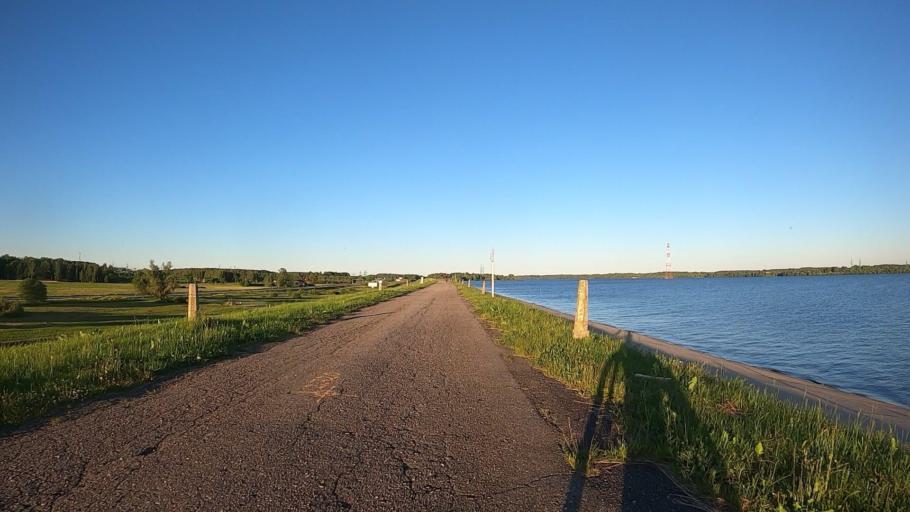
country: LV
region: Salaspils
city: Salaspils
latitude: 56.8467
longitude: 24.3503
